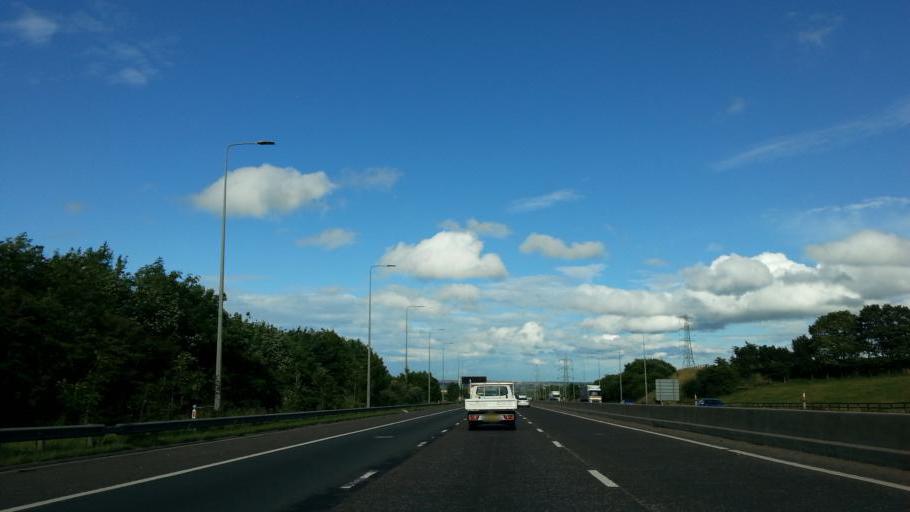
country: GB
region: England
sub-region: Calderdale
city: Brighouse
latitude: 53.6798
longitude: -1.8032
